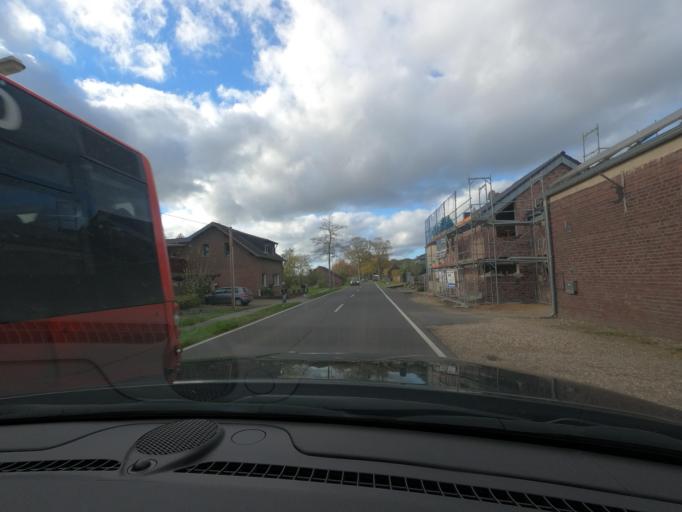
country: DE
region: North Rhine-Westphalia
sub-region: Regierungsbezirk Dusseldorf
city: Schwalmtal
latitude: 51.2533
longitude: 6.3074
